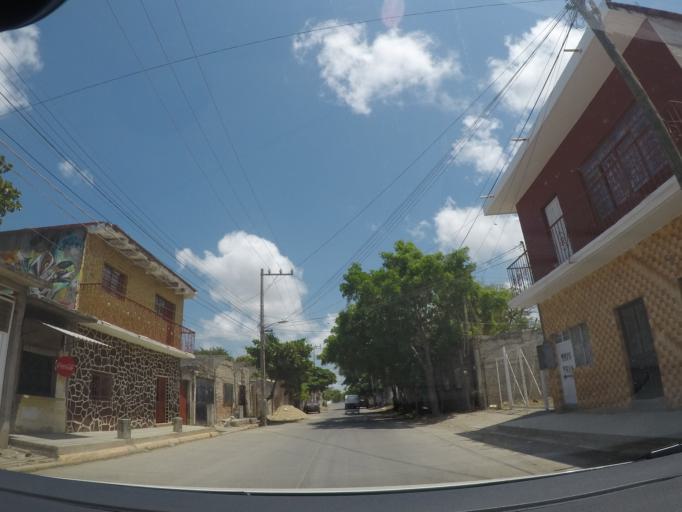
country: MX
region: Oaxaca
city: Juchitan de Zaragoza
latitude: 16.4396
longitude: -95.0163
